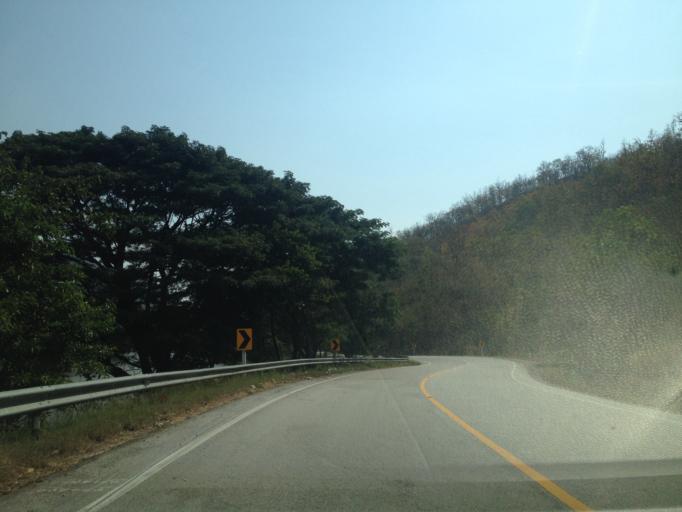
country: TH
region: Chiang Mai
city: Hot
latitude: 18.2153
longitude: 98.5816
